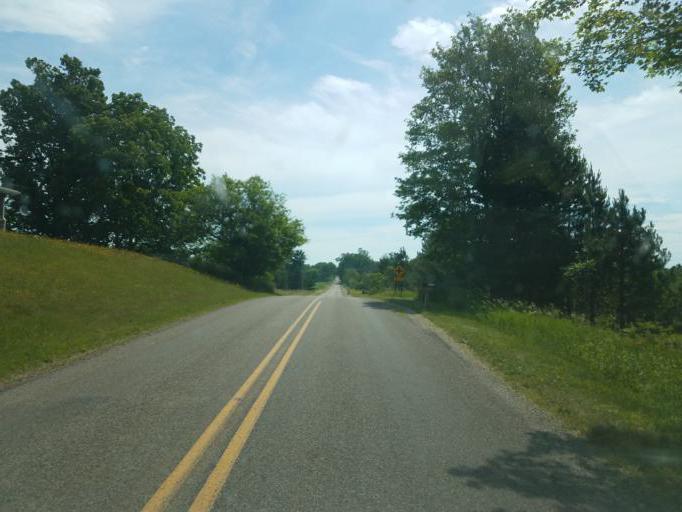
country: US
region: Michigan
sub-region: Barry County
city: Nashville
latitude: 42.6834
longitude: -85.0179
